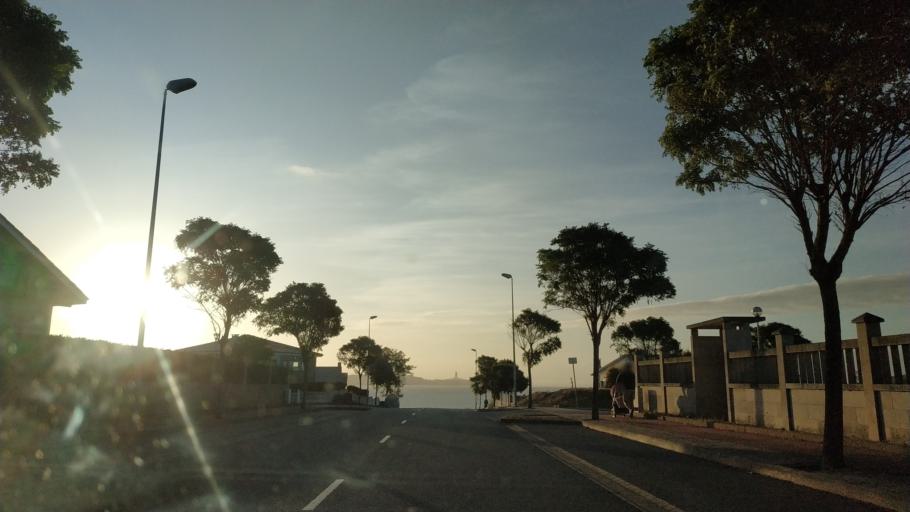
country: ES
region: Galicia
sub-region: Provincia da Coruna
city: Oleiros
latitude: 43.3710
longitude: -8.3425
